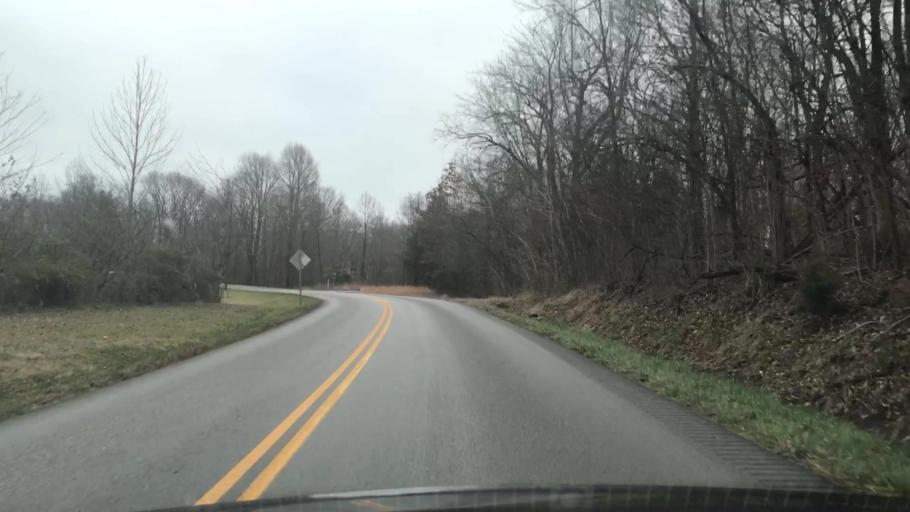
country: US
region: Kentucky
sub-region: Barren County
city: Glasgow
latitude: 36.8837
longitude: -85.7920
